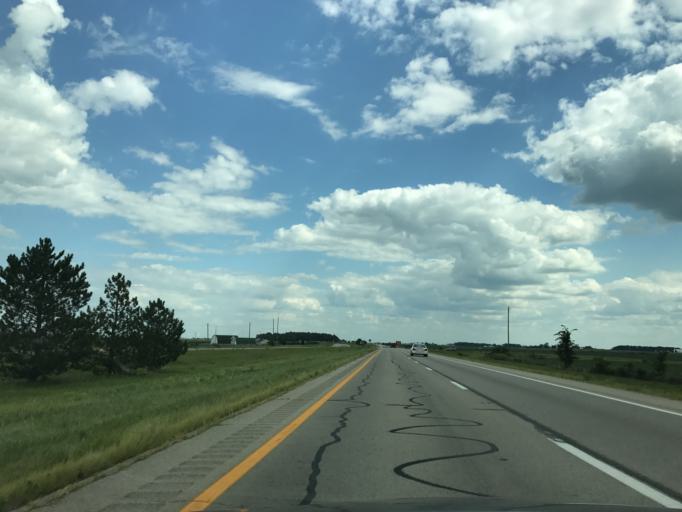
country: US
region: Ohio
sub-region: Van Wert County
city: Convoy
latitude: 40.9765
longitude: -84.7637
